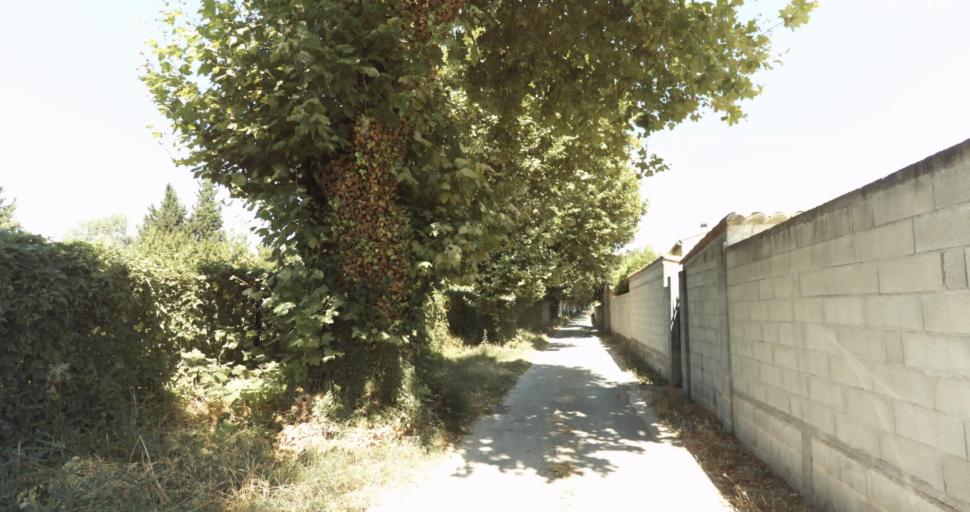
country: FR
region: Provence-Alpes-Cote d'Azur
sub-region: Departement du Vaucluse
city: Monteux
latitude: 44.0363
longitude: 4.9852
